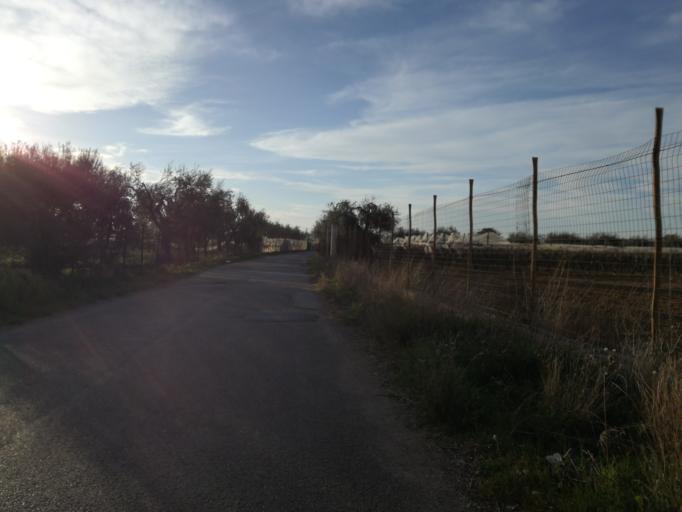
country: IT
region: Apulia
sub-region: Provincia di Bari
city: Valenzano
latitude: 41.0508
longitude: 16.9013
